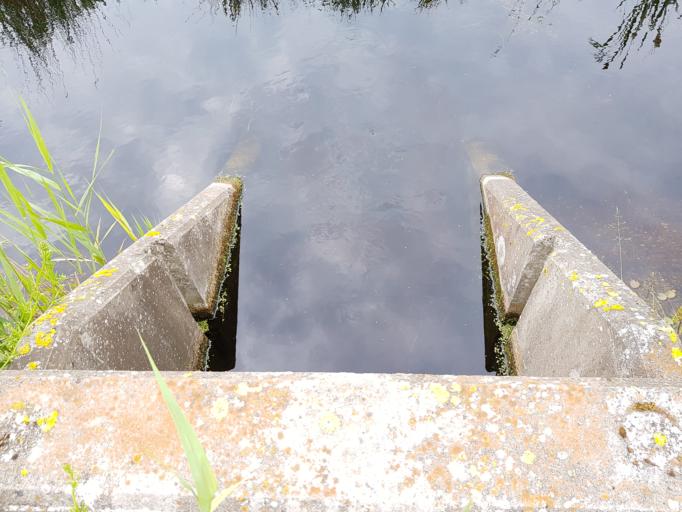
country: NL
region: Friesland
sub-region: Gemeente Boarnsterhim
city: Warten
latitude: 53.1379
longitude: 5.9229
